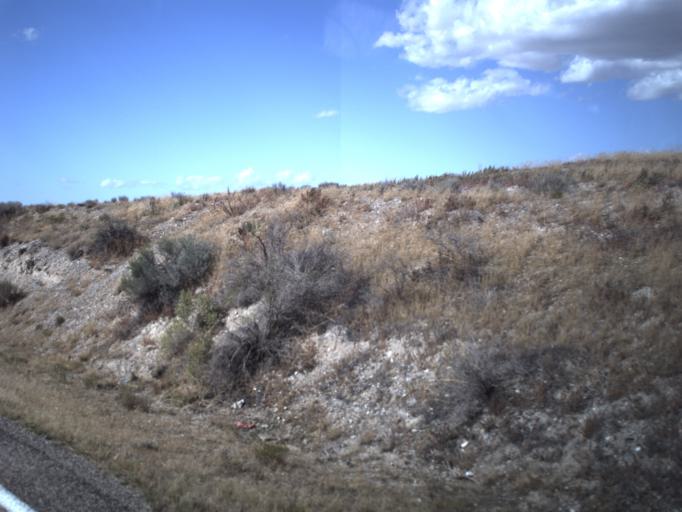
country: US
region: Utah
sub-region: Beaver County
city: Milford
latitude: 38.7428
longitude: -112.9564
